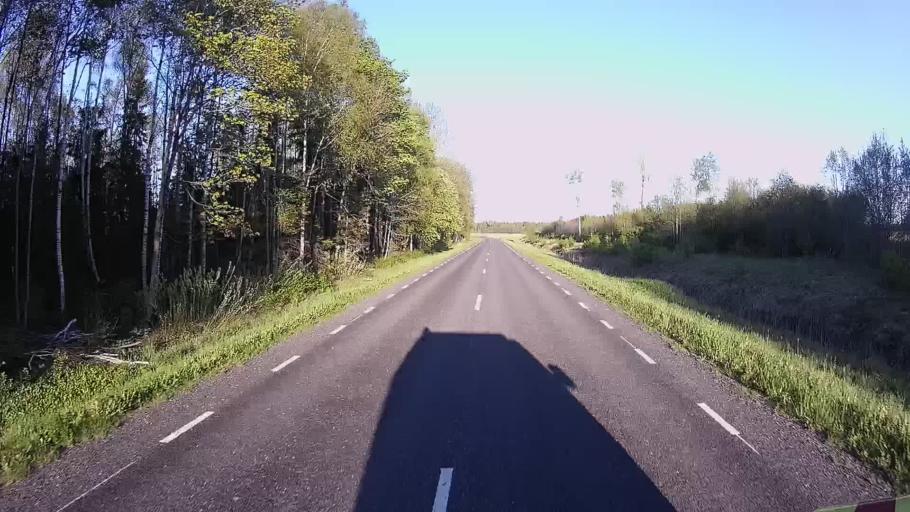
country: EE
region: Jogevamaa
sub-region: Poltsamaa linn
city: Poltsamaa
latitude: 58.5234
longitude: 25.9653
